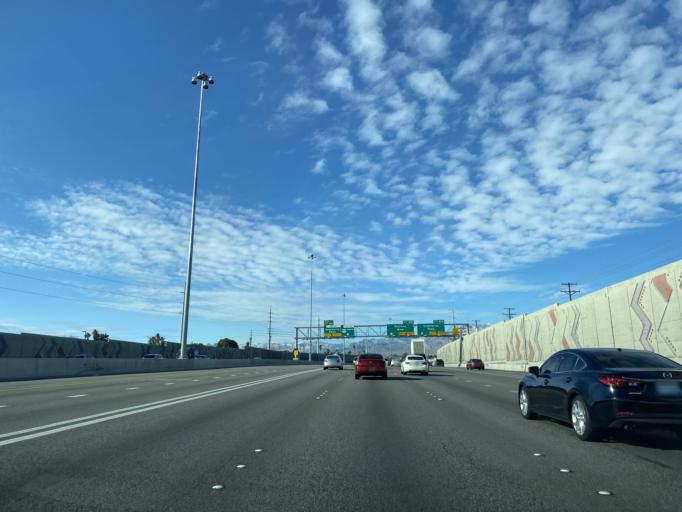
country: US
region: Nevada
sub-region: Clark County
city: Spring Valley
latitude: 36.1754
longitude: -115.2353
